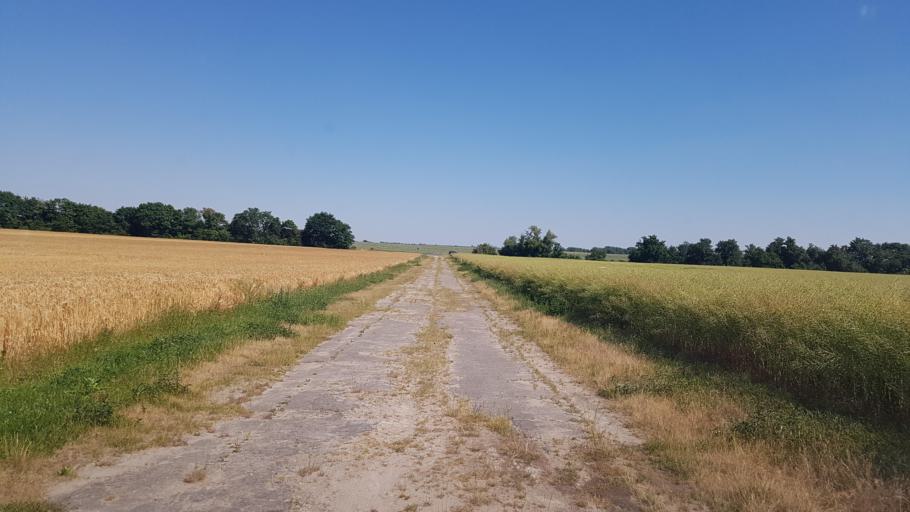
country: DE
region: Saxony-Anhalt
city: Seyda
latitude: 51.9639
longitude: 12.8965
